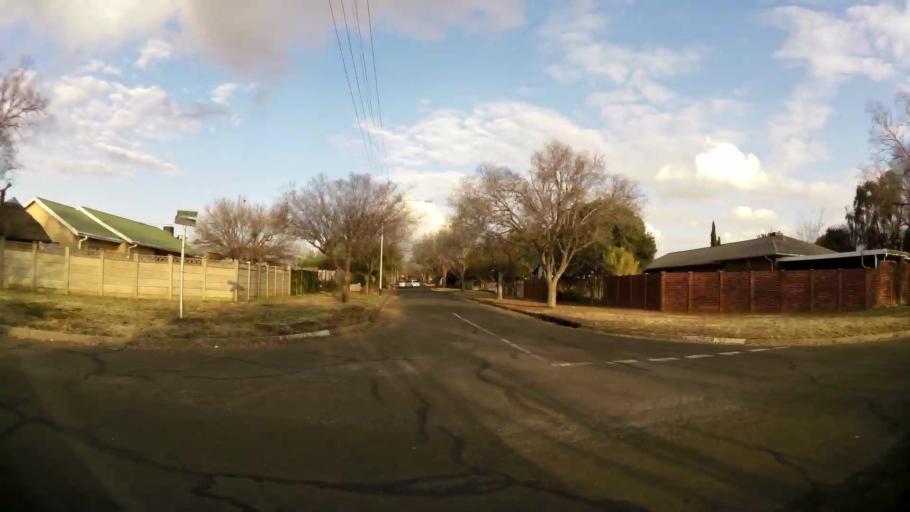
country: ZA
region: Orange Free State
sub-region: Mangaung Metropolitan Municipality
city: Bloemfontein
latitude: -29.1389
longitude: 26.1953
